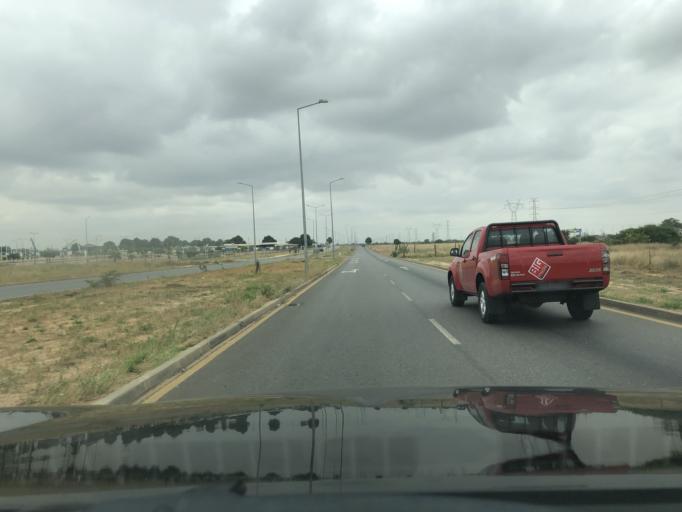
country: AO
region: Luanda
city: Luanda
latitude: -8.9758
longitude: 13.2855
